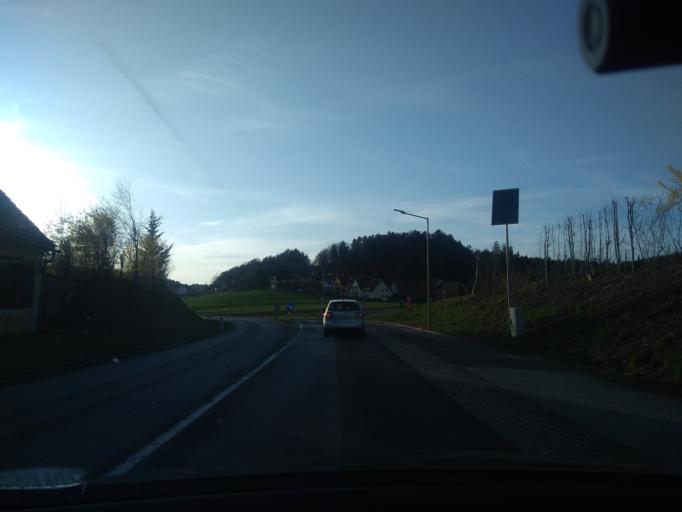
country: AT
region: Styria
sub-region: Politischer Bezirk Leibnitz
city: Empersdorf
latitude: 46.9828
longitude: 15.5636
